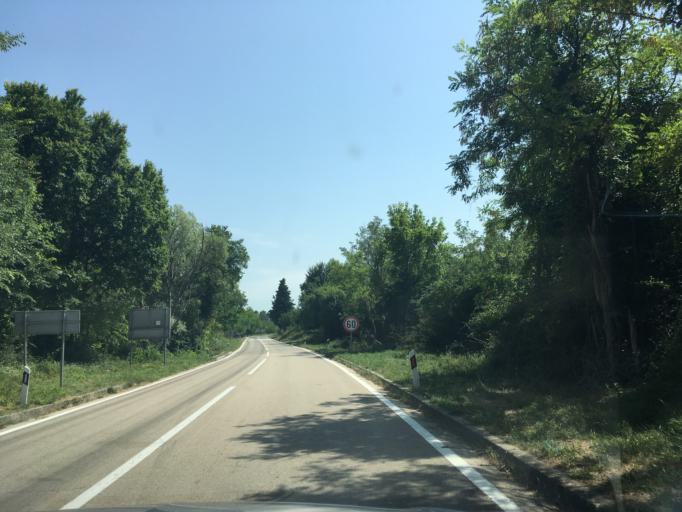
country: HR
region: Sibensko-Kniniska
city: Zaton
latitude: 43.9283
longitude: 15.8124
